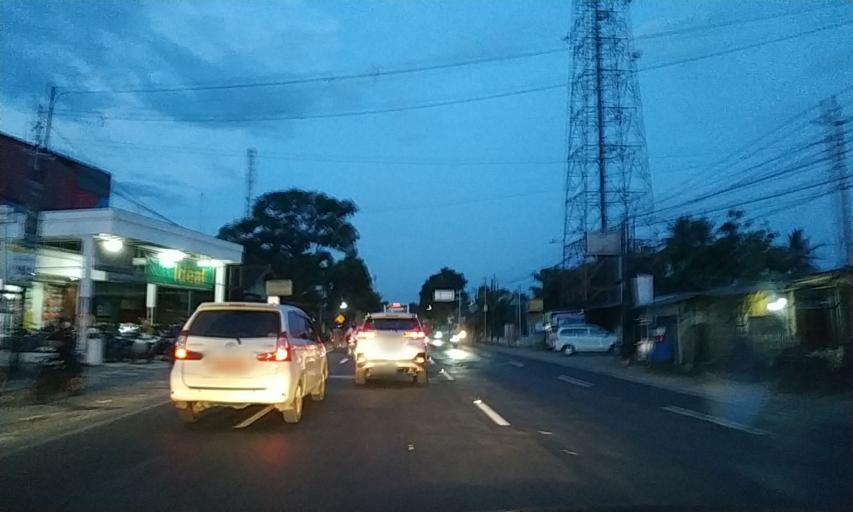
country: ID
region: Daerah Istimewa Yogyakarta
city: Godean
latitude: -7.8142
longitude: 110.2573
